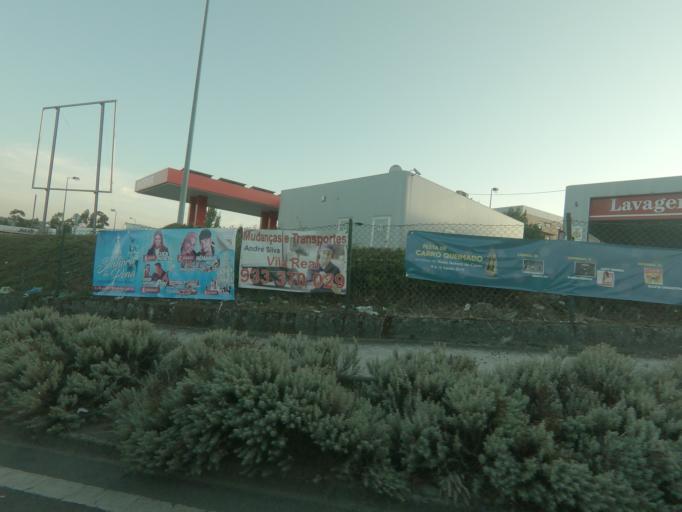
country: PT
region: Vila Real
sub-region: Vila Real
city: Vila Real
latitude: 41.3095
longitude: -7.7355
